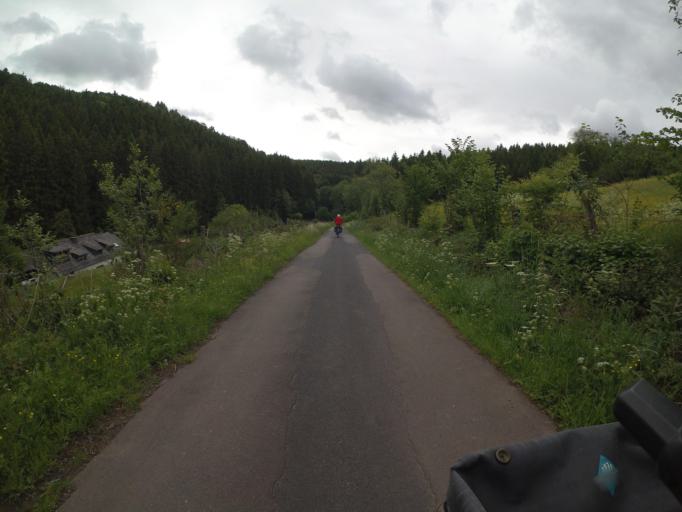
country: DE
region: North Rhine-Westphalia
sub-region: Regierungsbezirk Koln
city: Hellenthal
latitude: 50.4300
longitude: 6.4063
